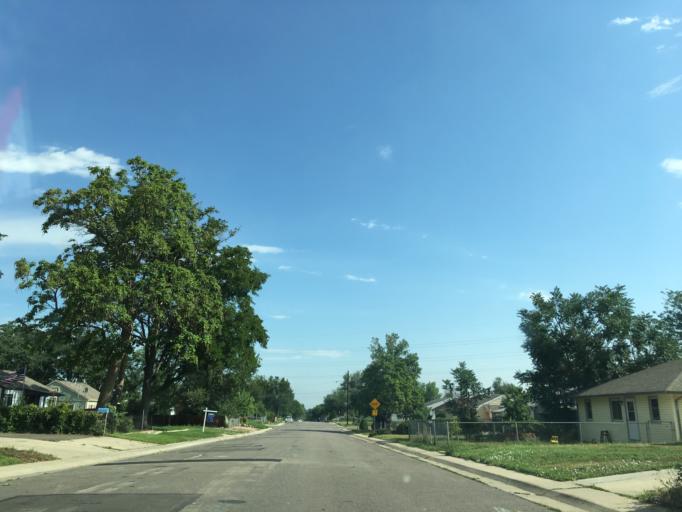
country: US
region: Colorado
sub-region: Jefferson County
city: Lakewood
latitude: 39.6975
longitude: -105.0367
